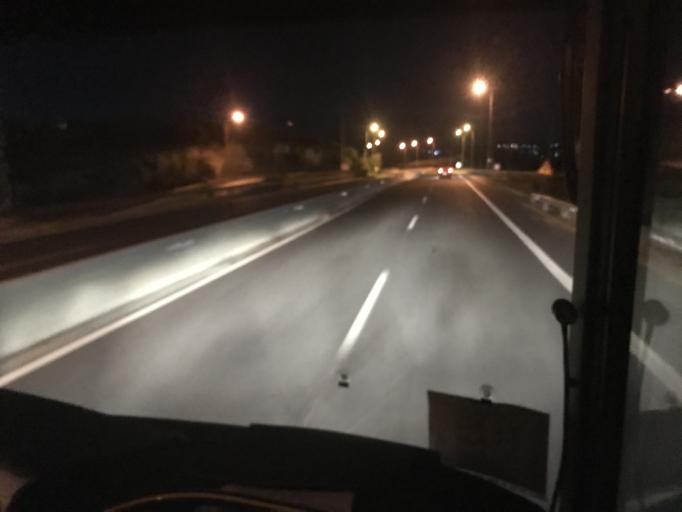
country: GR
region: Crete
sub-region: Nomos Irakleiou
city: Skalanion
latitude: 35.2642
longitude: 25.1829
